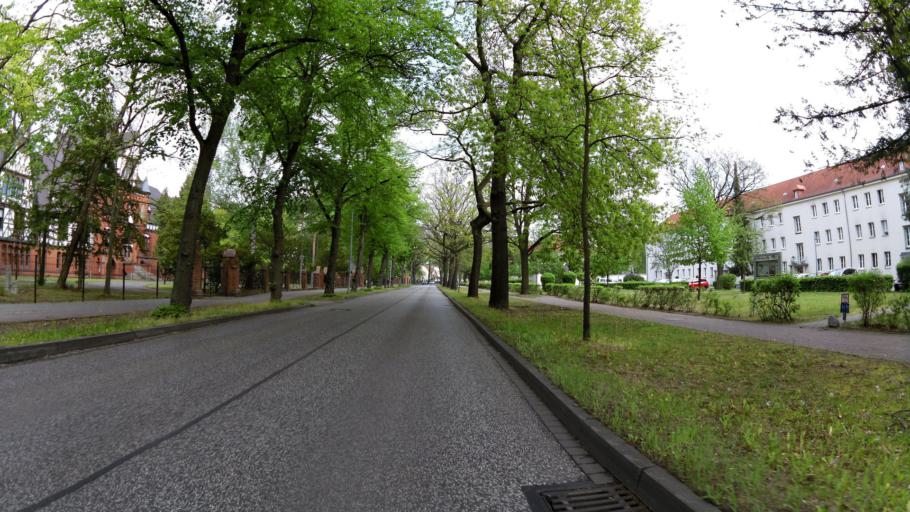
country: DE
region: Brandenburg
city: Konigs Wusterhausen
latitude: 52.2898
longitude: 13.6177
